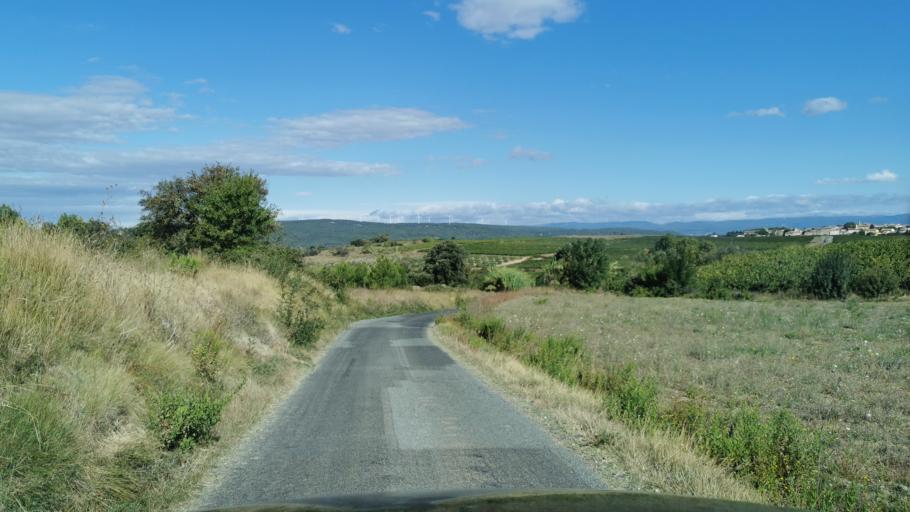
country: FR
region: Languedoc-Roussillon
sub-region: Departement de l'Aude
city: Ginestas
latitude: 43.2610
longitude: 2.8452
